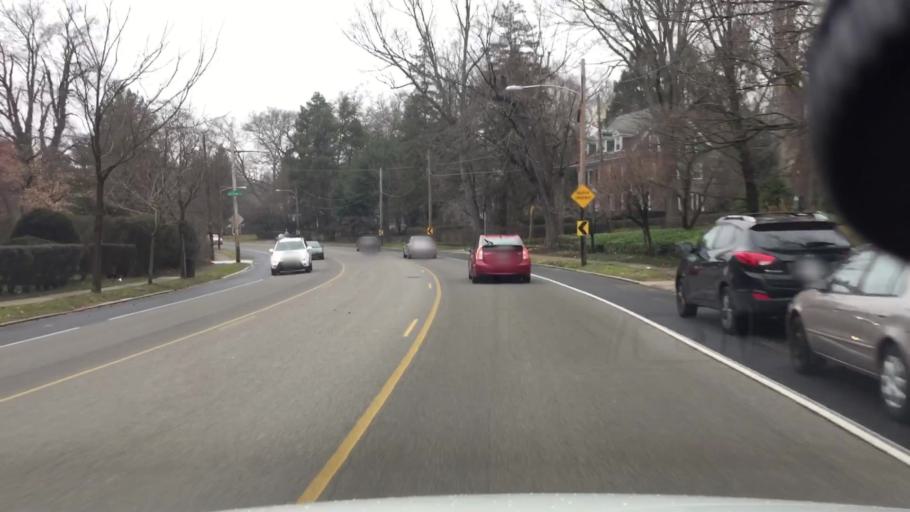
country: US
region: Pennsylvania
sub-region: Montgomery County
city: Wyndmoor
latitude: 40.0471
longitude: -75.1921
